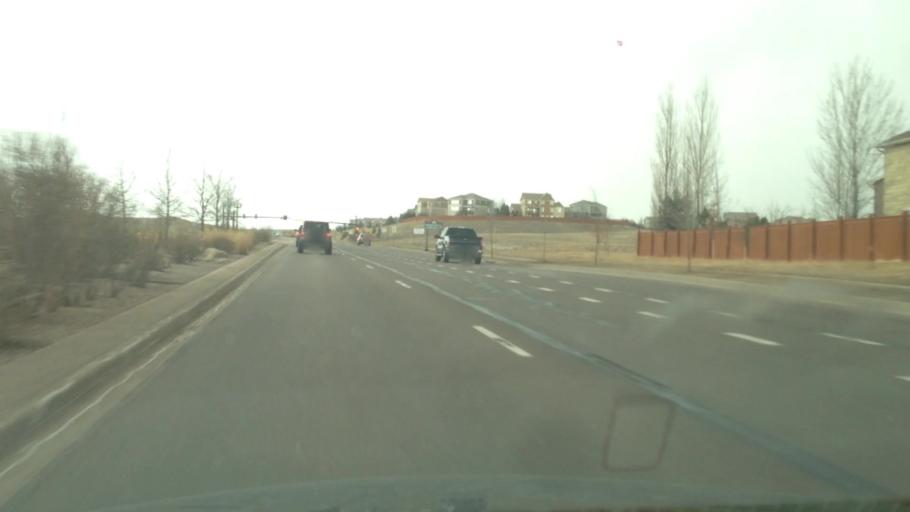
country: US
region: Colorado
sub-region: Douglas County
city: Stonegate
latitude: 39.4931
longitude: -104.7980
